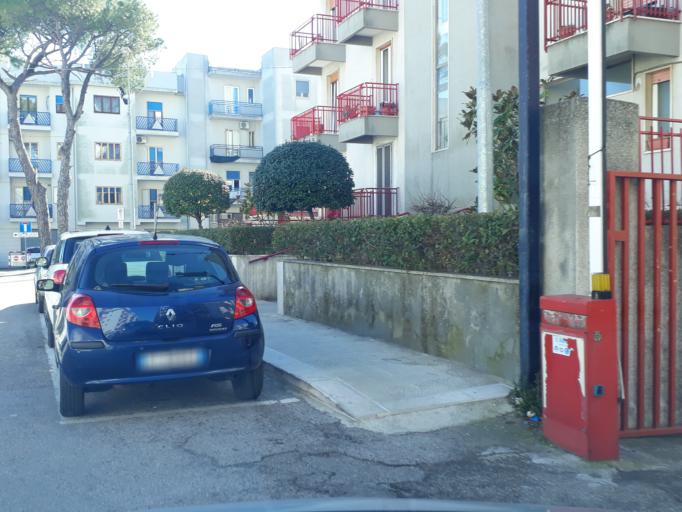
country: IT
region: Apulia
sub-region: Provincia di Taranto
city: Martina Franca
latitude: 40.7024
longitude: 17.3466
